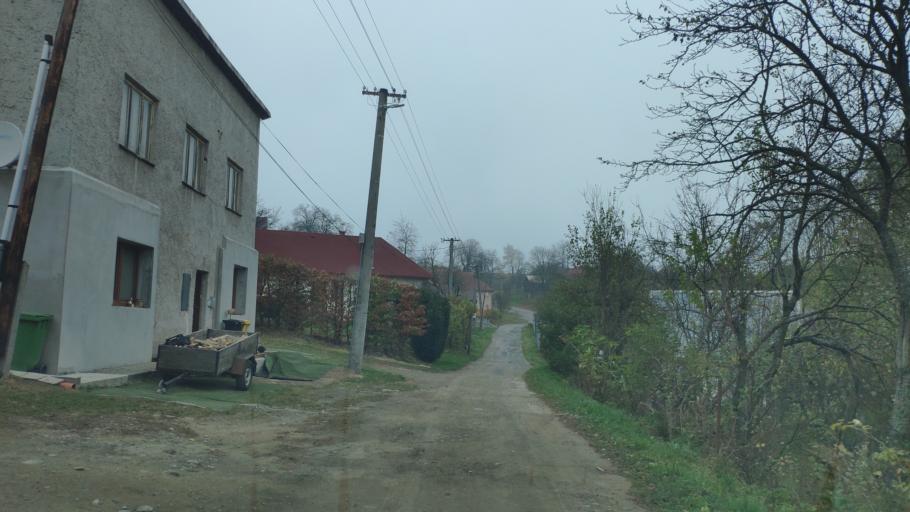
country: SK
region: Presovsky
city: Sabinov
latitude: 49.1462
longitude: 21.2387
